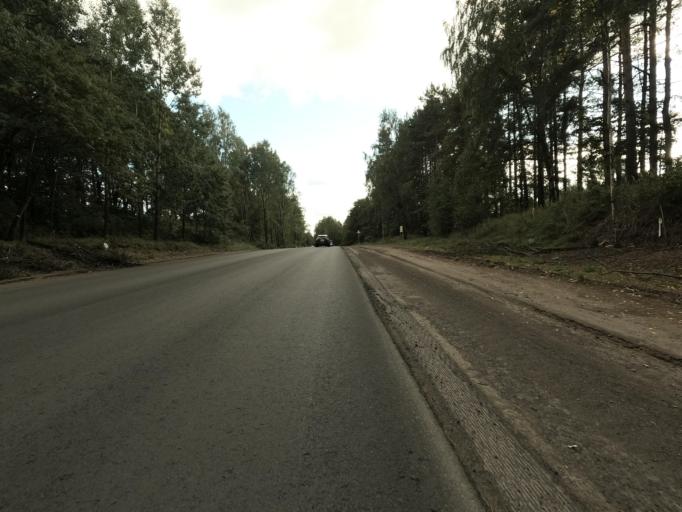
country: RU
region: Leningrad
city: Koltushi
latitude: 59.9505
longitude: 30.6569
